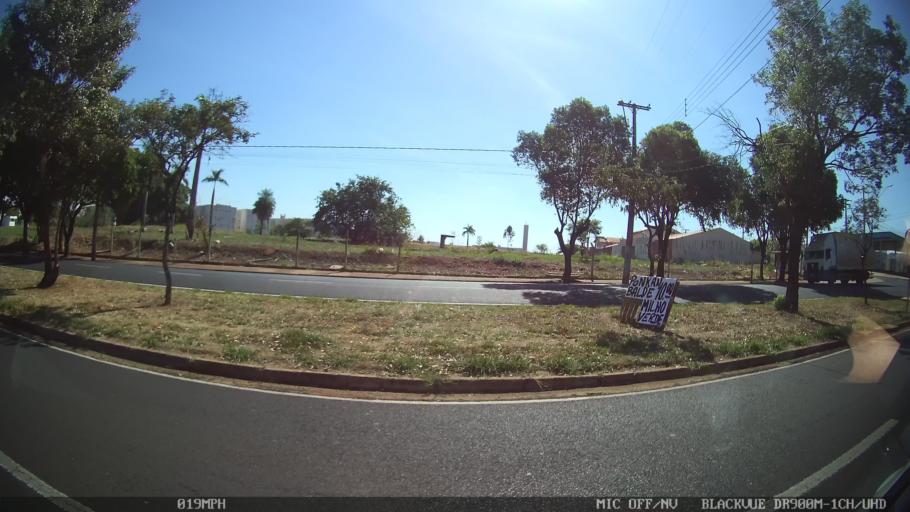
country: BR
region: Sao Paulo
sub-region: Sao Jose Do Rio Preto
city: Sao Jose do Rio Preto
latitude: -20.7803
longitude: -49.3759
